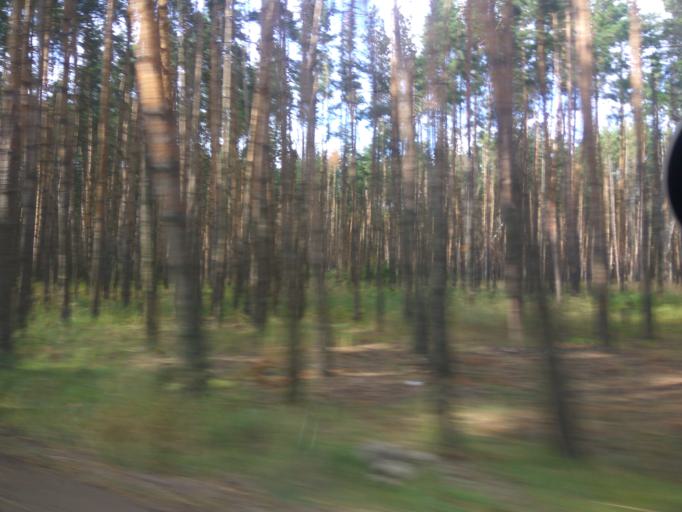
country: RU
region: Moskovskaya
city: Bronnitsy
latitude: 55.4712
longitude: 38.2725
